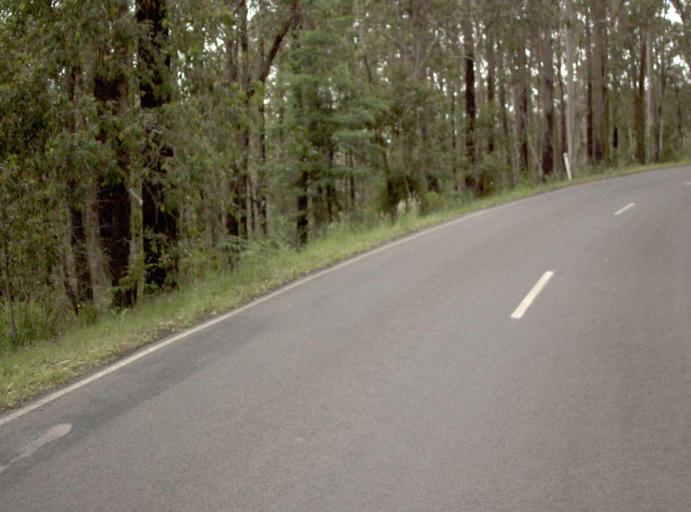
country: AU
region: Victoria
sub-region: Latrobe
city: Moe
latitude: -37.9332
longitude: 146.1158
